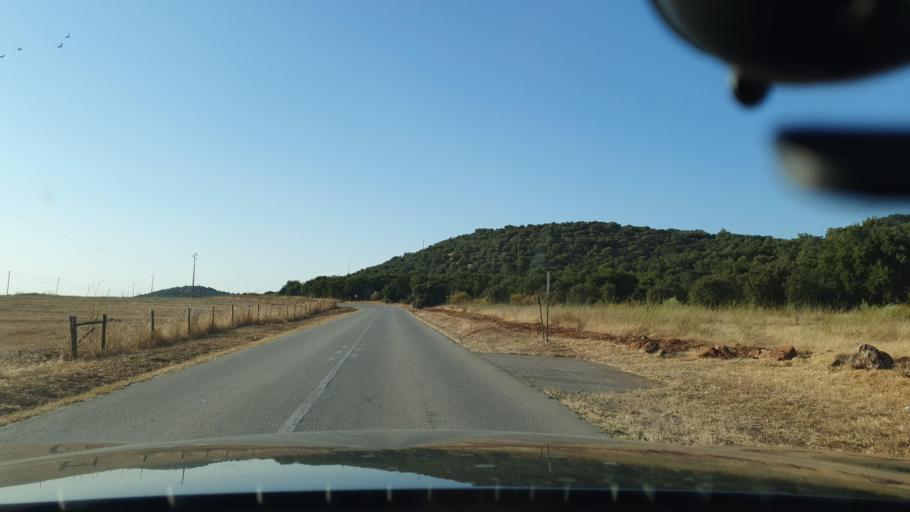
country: PT
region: Evora
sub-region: Estremoz
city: Estremoz
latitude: 38.8832
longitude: -7.6454
